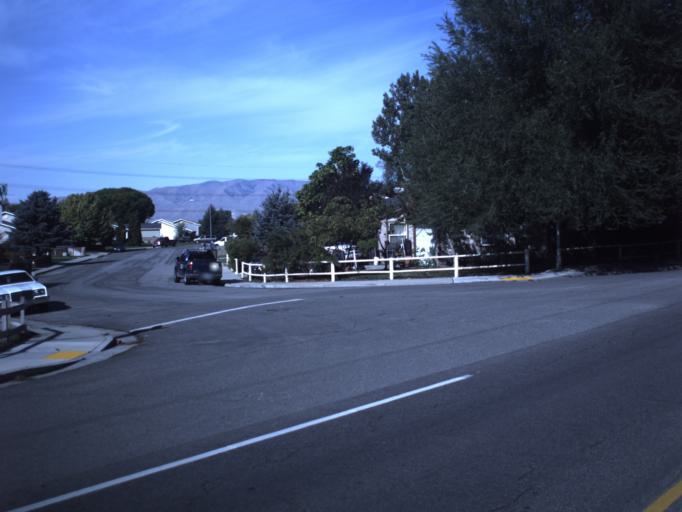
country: US
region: Utah
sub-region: Utah County
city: Provo
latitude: 40.2463
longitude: -111.6991
